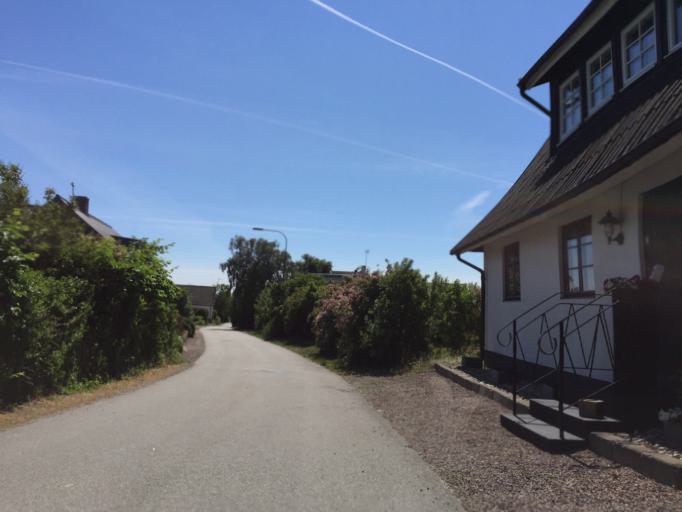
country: SE
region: Skane
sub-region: Trelleborgs Kommun
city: Skare
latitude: 55.3753
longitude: 13.0823
